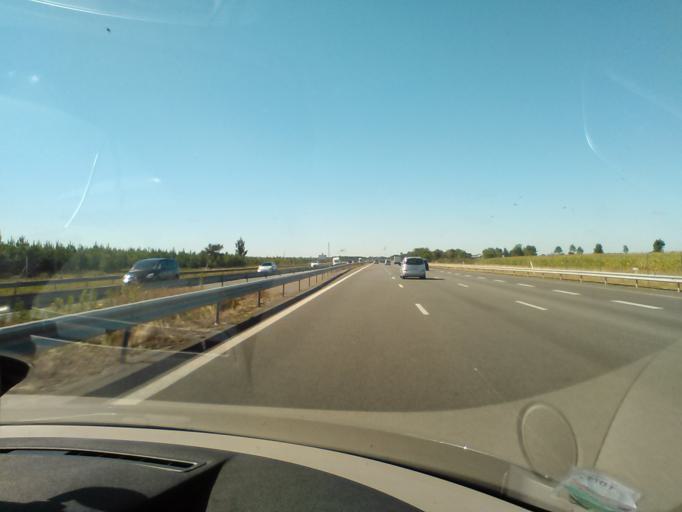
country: FR
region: Aquitaine
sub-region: Departement des Landes
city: Labouheyre
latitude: 44.2501
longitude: -0.9042
